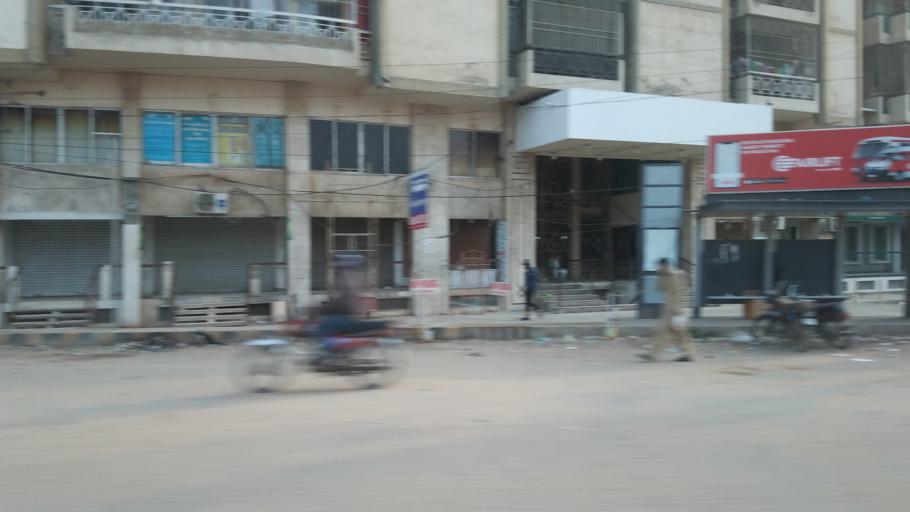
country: PK
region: Sindh
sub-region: Karachi District
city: Karachi
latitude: 24.9312
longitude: 67.0864
